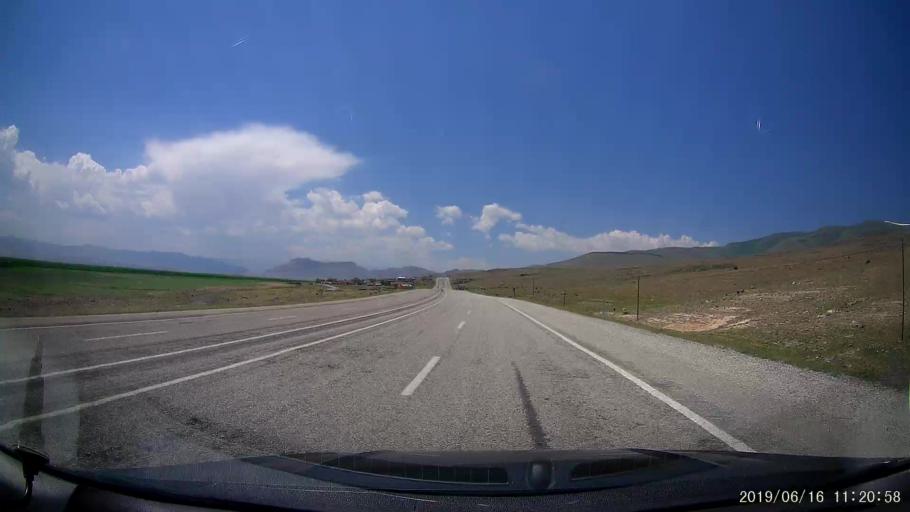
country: TR
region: Agri
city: Dogubayazit
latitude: 39.6982
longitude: 44.0787
